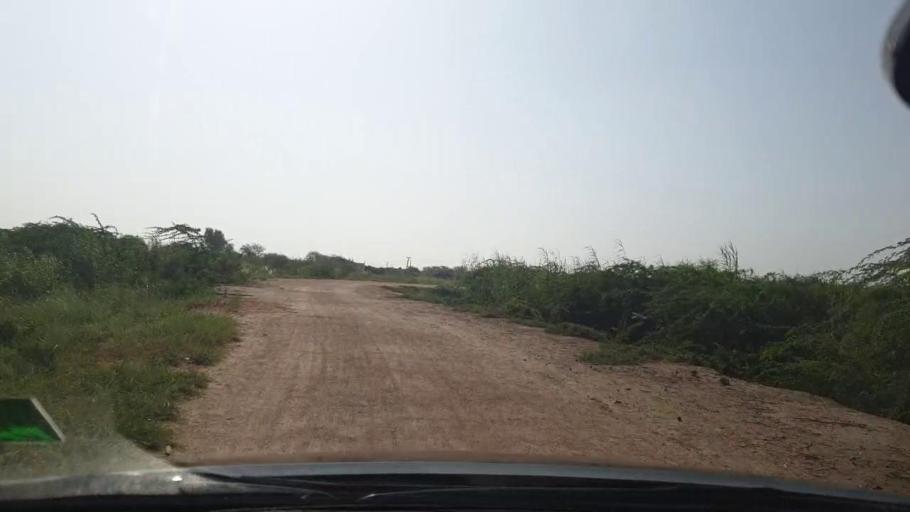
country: PK
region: Sindh
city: Tando Bago
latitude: 24.6969
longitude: 69.0201
